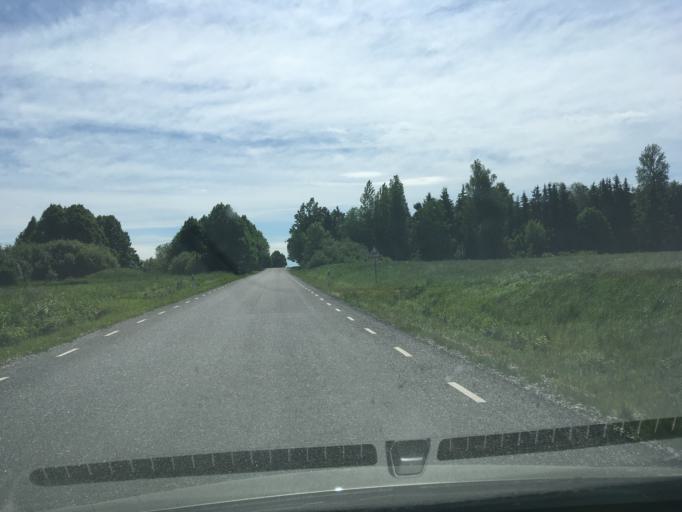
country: EE
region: Paernumaa
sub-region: Audru vald
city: Audru
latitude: 58.4417
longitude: 24.3941
